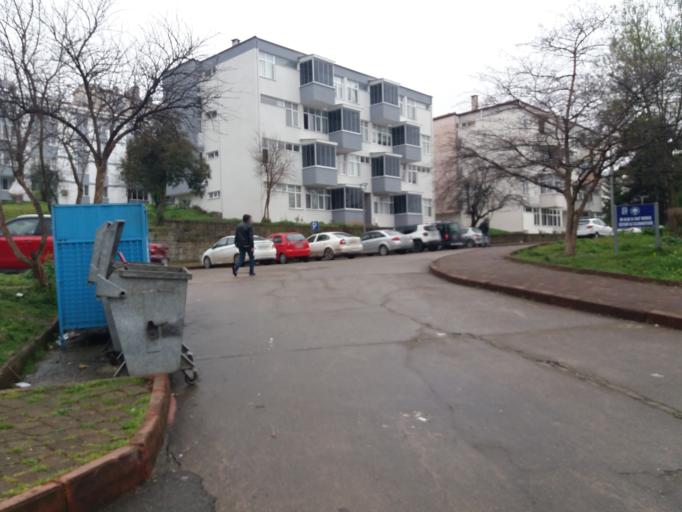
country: TR
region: Trabzon
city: Trabzon
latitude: 40.9958
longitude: 39.7673
